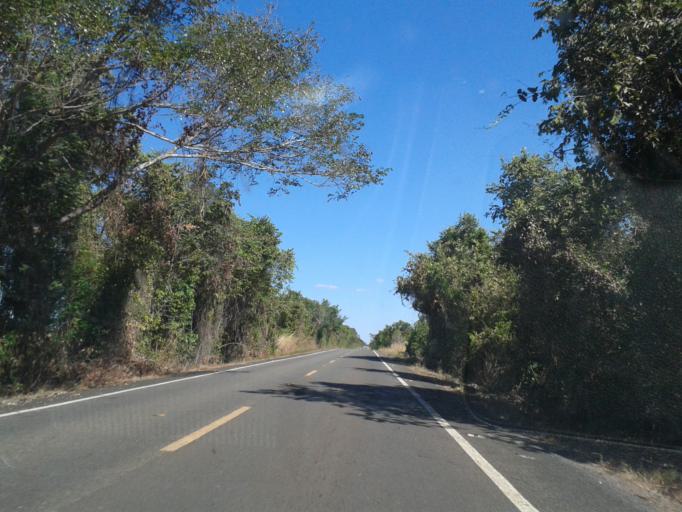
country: BR
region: Goias
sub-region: Sao Miguel Do Araguaia
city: Sao Miguel do Araguaia
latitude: -13.7166
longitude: -50.3338
